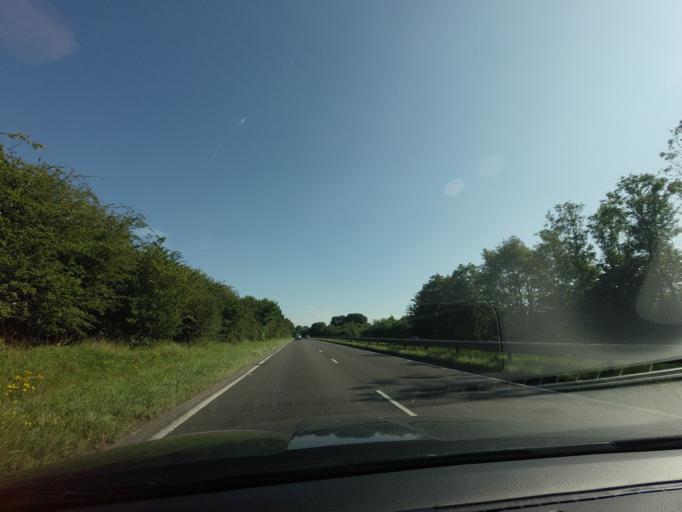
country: GB
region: England
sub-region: Derbyshire
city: Chesterfield
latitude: 53.2177
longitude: -1.3958
